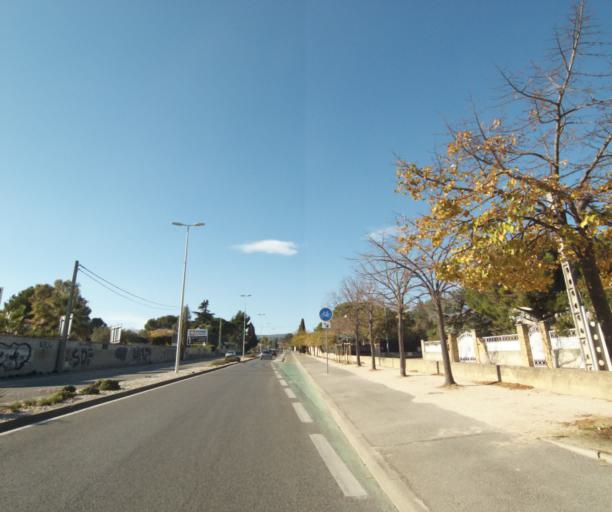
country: FR
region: Provence-Alpes-Cote d'Azur
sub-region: Departement des Bouches-du-Rhone
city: La Ciotat
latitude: 43.1919
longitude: 5.6175
